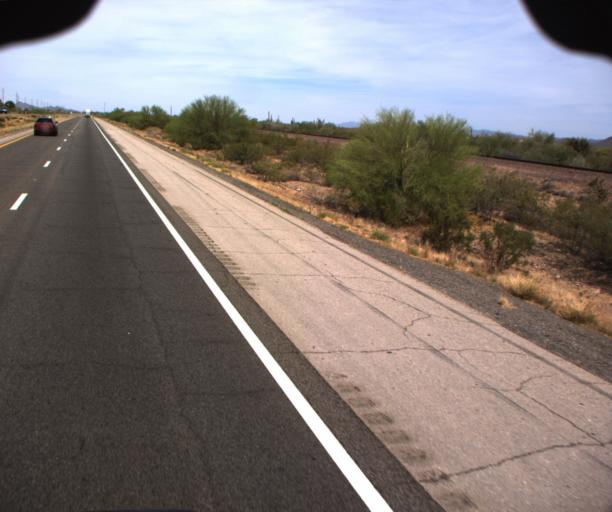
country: US
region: Arizona
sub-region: Maricopa County
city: Wickenburg
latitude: 33.8179
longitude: -112.5798
